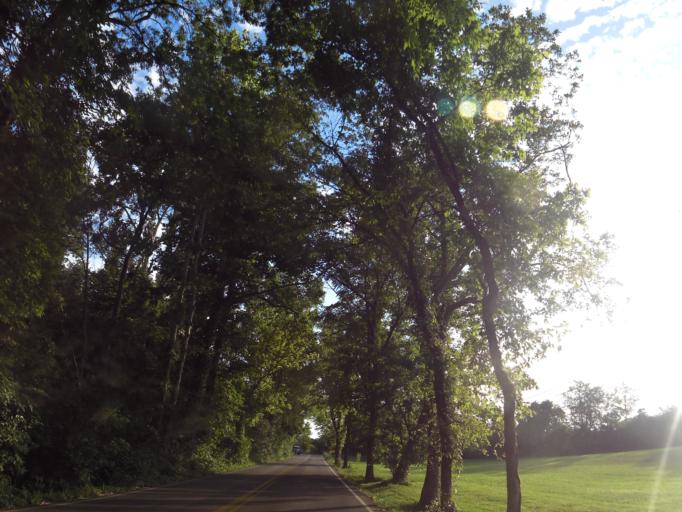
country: US
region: Tennessee
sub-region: Knox County
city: Knoxville
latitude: 36.0343
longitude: -83.9683
